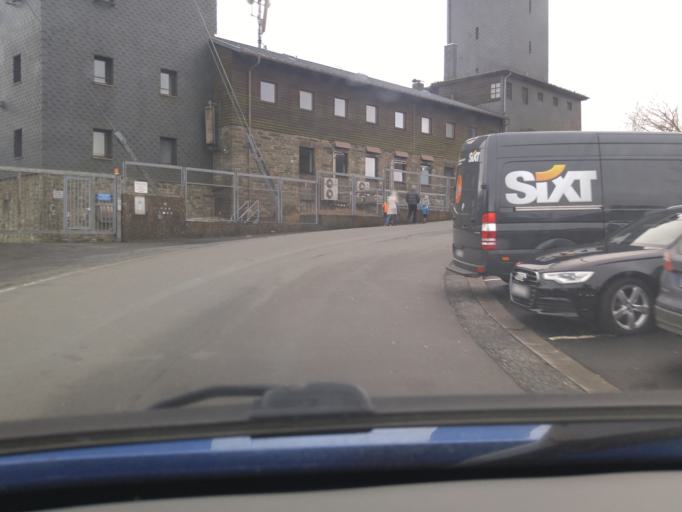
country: DE
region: Hesse
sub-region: Regierungsbezirk Darmstadt
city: Schmitten
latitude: 50.2325
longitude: 8.4586
